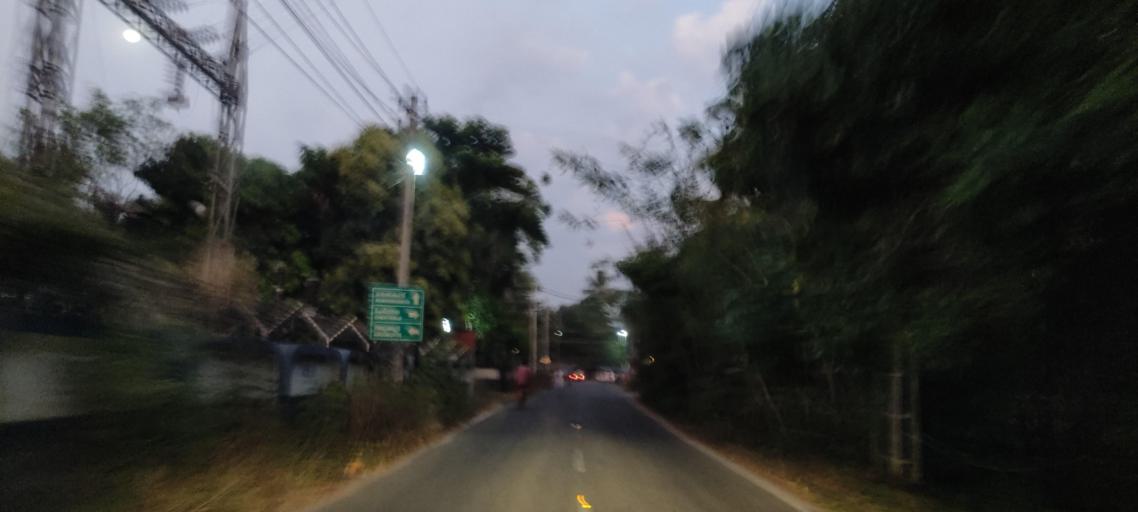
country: IN
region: Kerala
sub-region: Alappuzha
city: Kutiatodu
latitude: 9.7745
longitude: 76.3603
